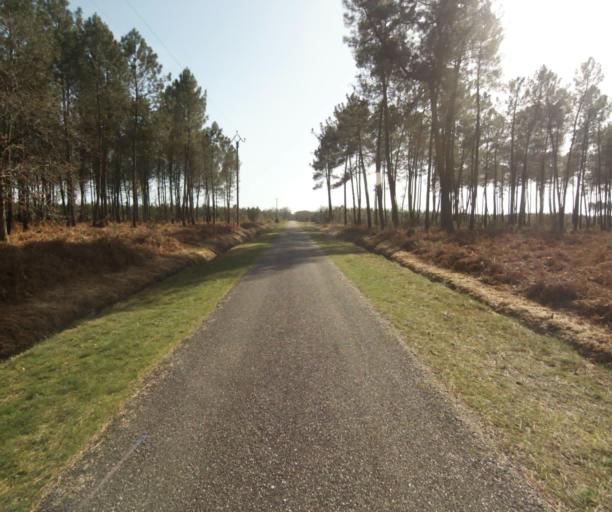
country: FR
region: Aquitaine
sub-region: Departement des Landes
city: Roquefort
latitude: 44.1336
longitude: -0.1942
